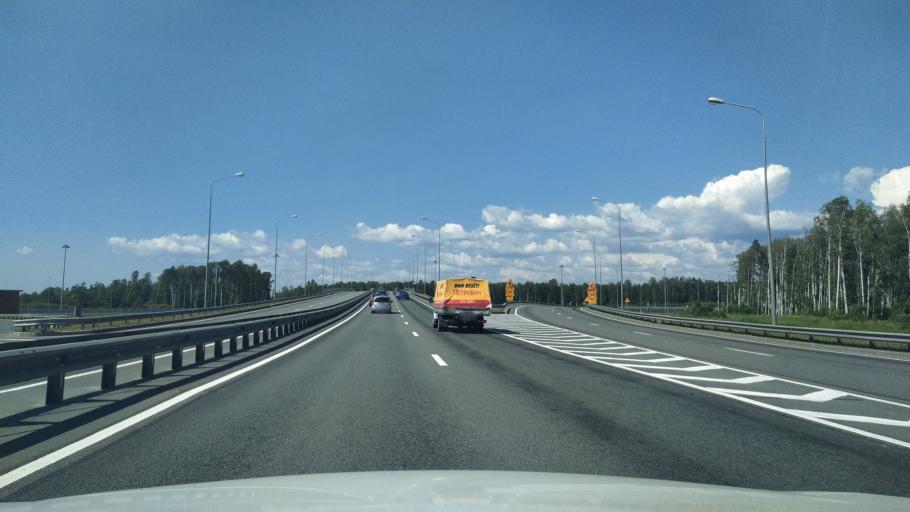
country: RU
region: St.-Petersburg
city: Levashovo
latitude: 60.0729
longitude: 30.1829
